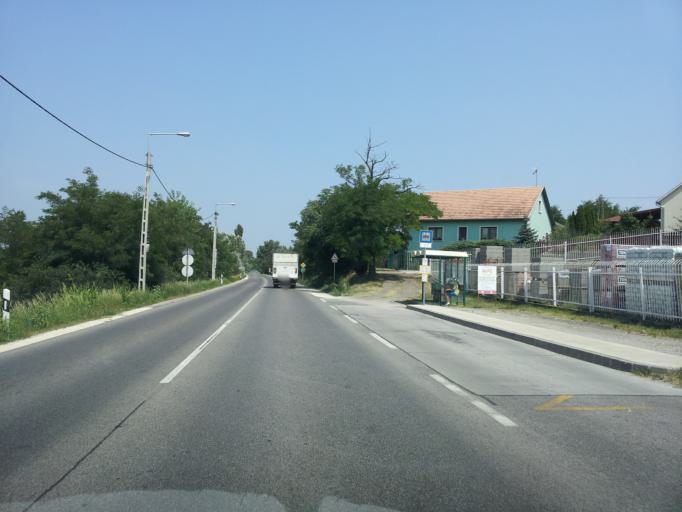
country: HU
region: Pest
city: Dunavarsany
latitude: 47.2923
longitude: 19.0301
